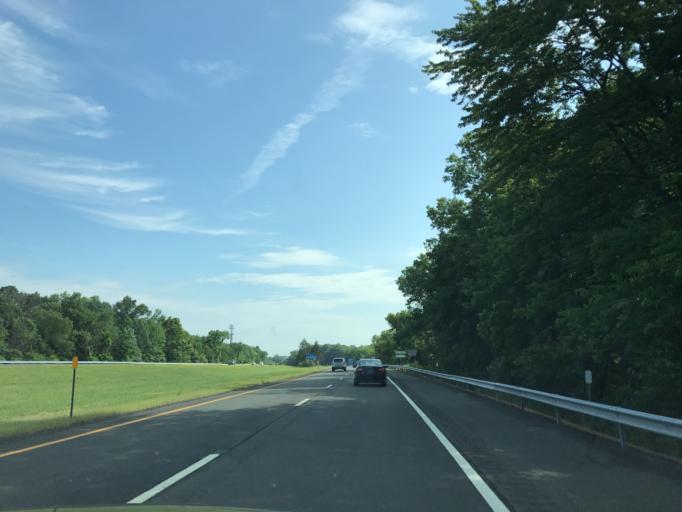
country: US
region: New York
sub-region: Rockland County
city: Chestnut Ridge
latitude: 41.0663
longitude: -74.0565
